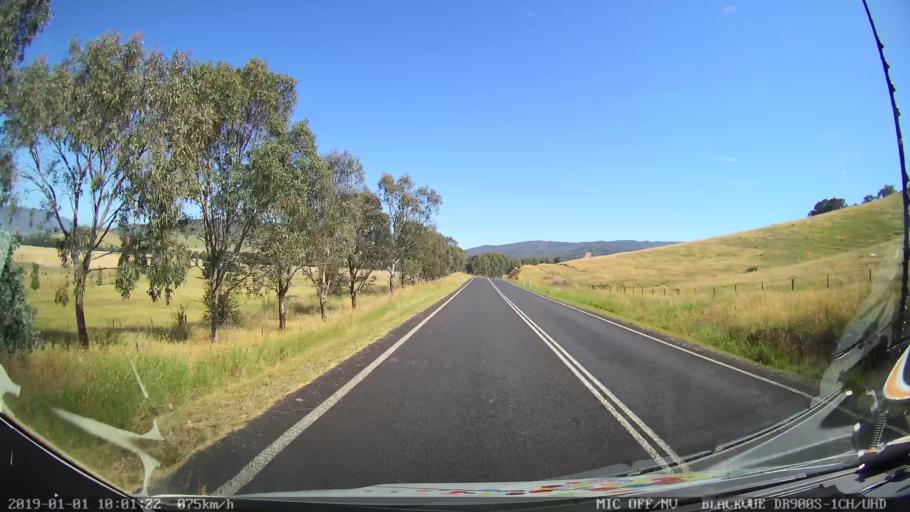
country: AU
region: New South Wales
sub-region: Snowy River
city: Jindabyne
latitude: -36.1923
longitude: 148.1013
